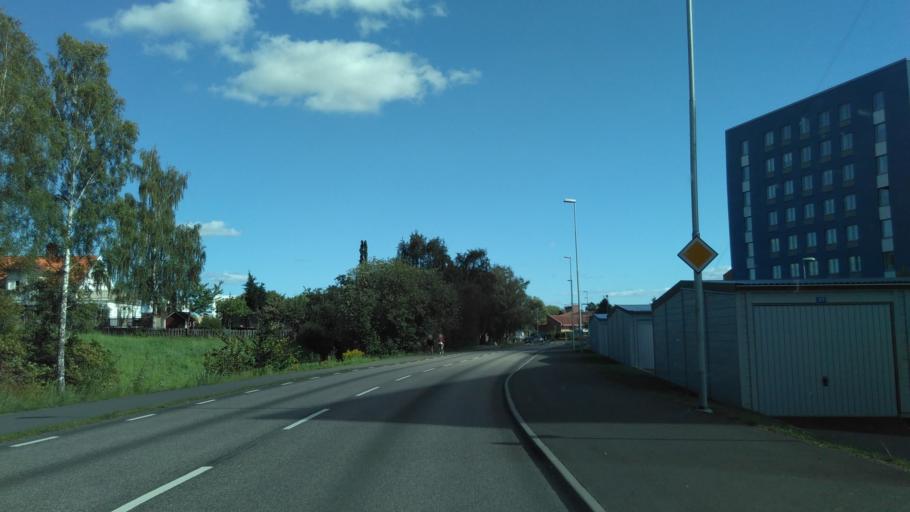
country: SE
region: Vaestra Goetaland
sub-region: Skovde Kommun
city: Skoevde
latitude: 58.4015
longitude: 13.8353
